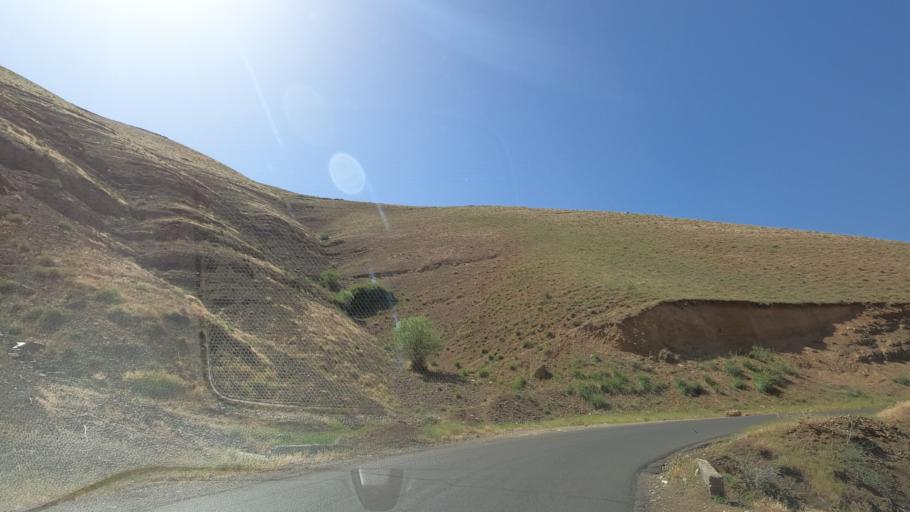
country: IR
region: Alborz
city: Karaj
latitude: 35.9318
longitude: 51.0867
